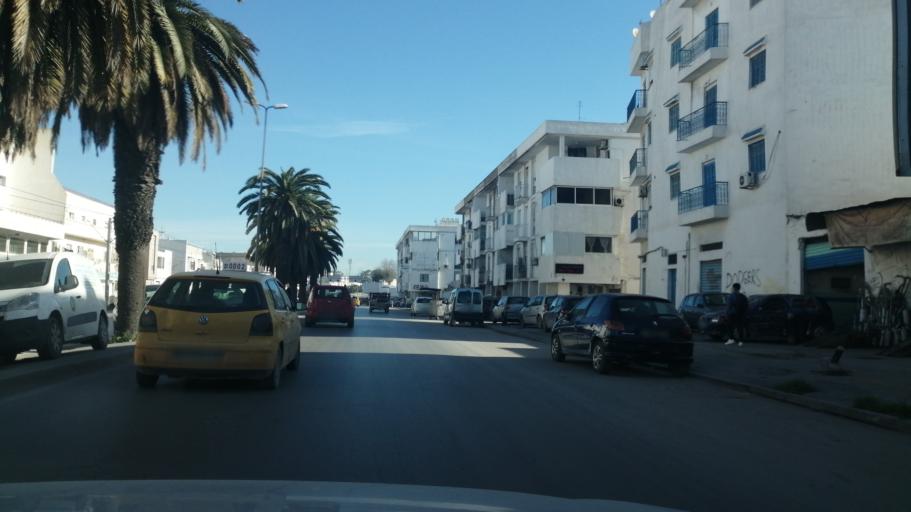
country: TN
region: Tunis
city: Tunis
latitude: 36.8110
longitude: 10.1654
